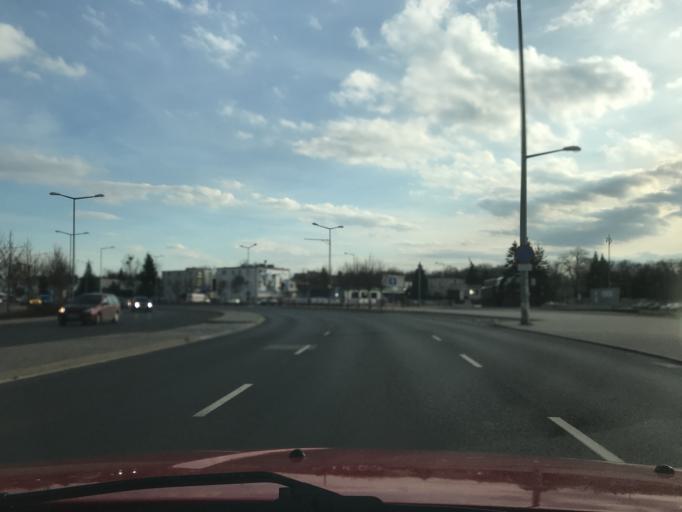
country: PL
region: Greater Poland Voivodeship
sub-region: Powiat poznanski
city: Lubon
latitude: 52.3977
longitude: 16.8617
